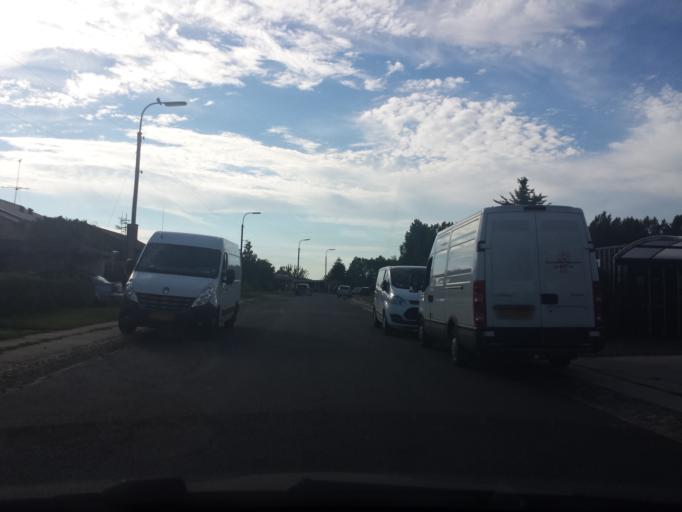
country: DK
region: Capital Region
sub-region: Ballerup Kommune
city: Ballerup
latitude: 55.7155
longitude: 12.3901
